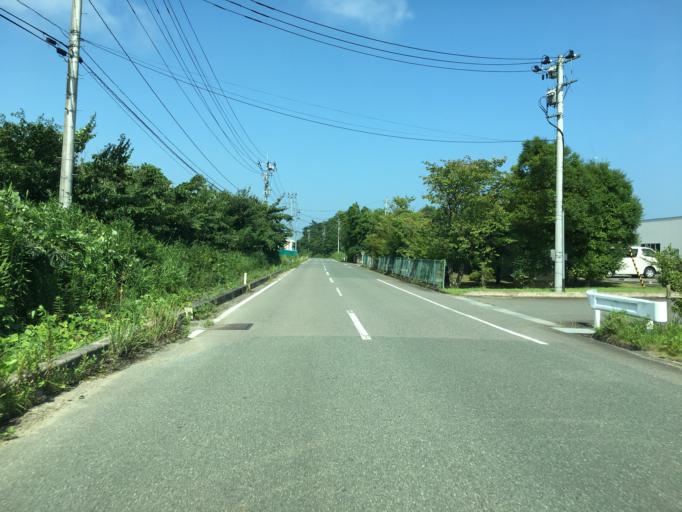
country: JP
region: Miyagi
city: Marumori
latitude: 37.9000
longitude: 140.8938
